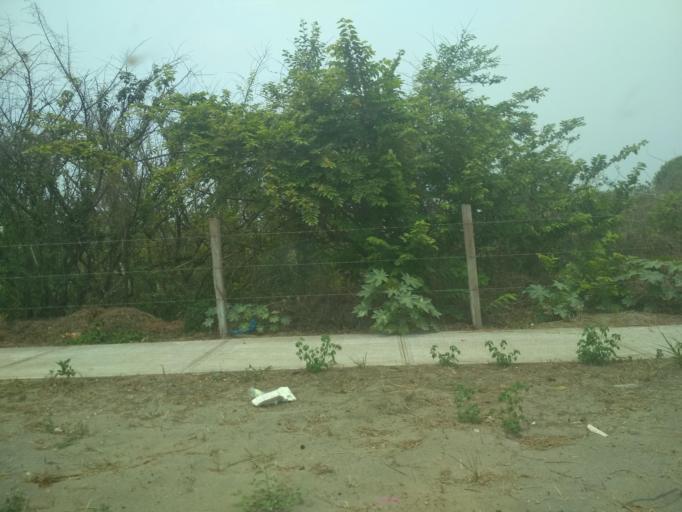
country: MX
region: Veracruz
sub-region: Alvarado
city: Playa de la Libertad
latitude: 19.0606
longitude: -96.0723
